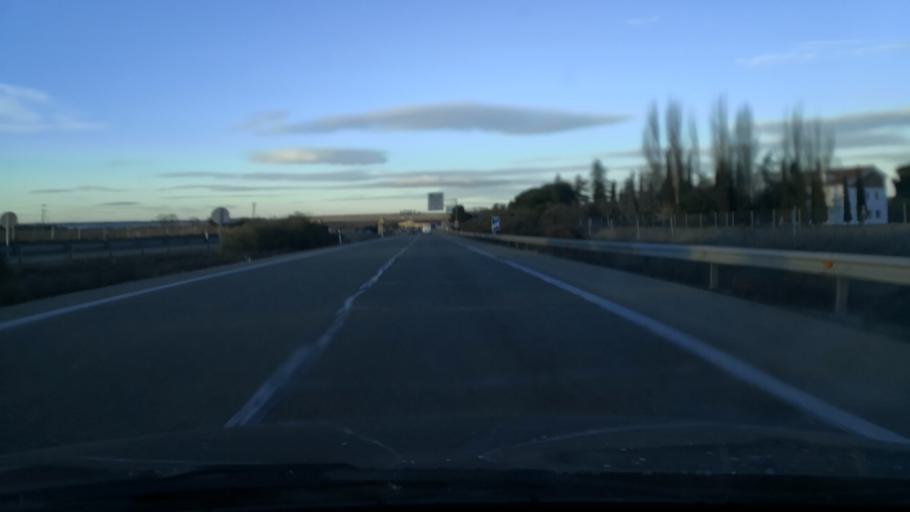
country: ES
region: Castille and Leon
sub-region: Provincia de Valladolid
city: Rueda
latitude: 41.4188
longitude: -4.9653
